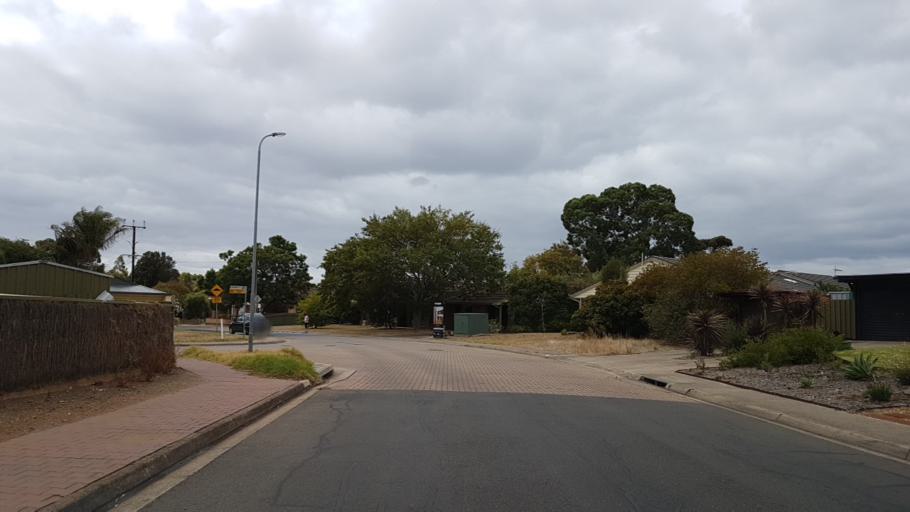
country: AU
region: South Australia
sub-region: Marion
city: Clovelly Park
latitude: -35.0030
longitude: 138.5695
